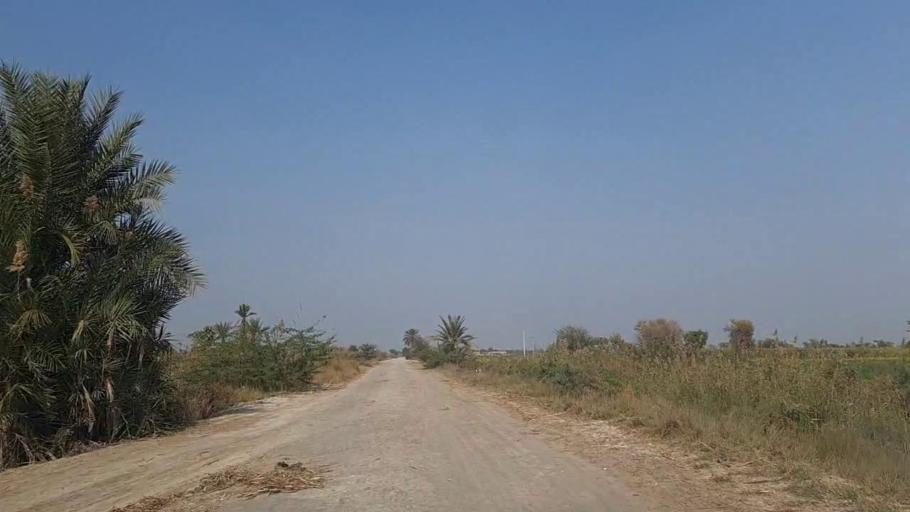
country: PK
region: Sindh
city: Daur
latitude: 26.4825
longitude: 68.4513
